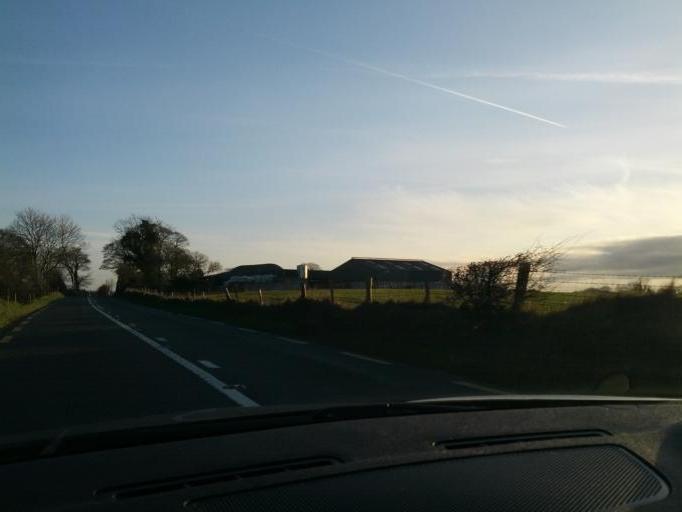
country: IE
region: Connaught
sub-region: Sligo
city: Tobercurry
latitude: 54.0660
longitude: -8.7099
